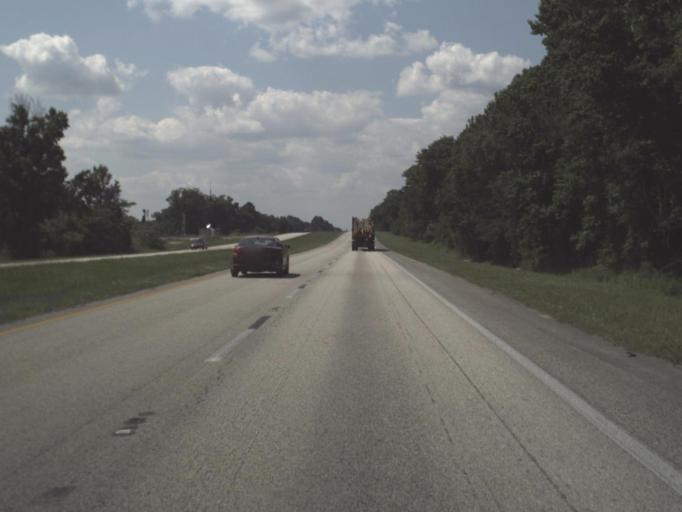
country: US
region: Florida
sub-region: Alachua County
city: Hawthorne
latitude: 29.6228
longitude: -82.0981
